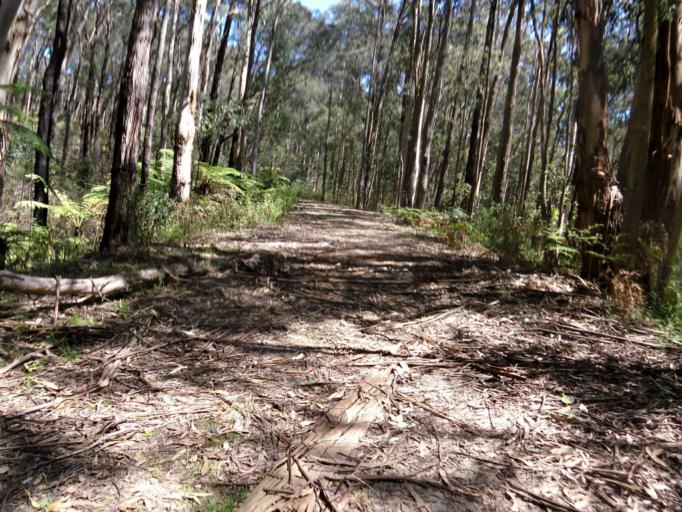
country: AU
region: Victoria
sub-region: Baw Baw
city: Warragul
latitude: -37.9040
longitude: 145.9764
